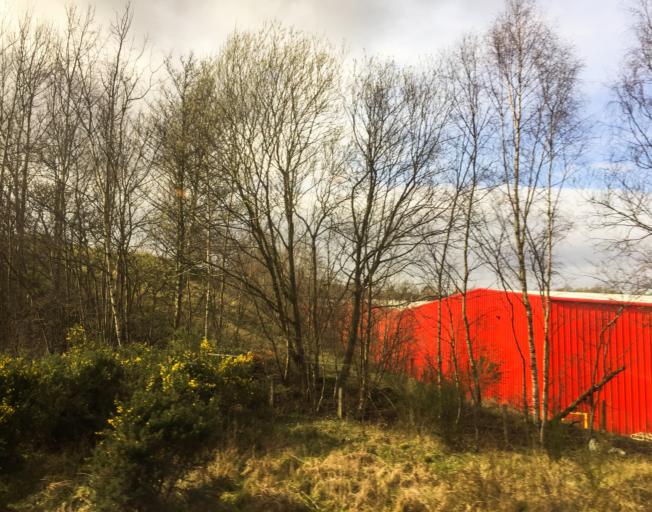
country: GB
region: Scotland
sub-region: East Dunbartonshire
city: Bearsden
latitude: 55.8956
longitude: -4.3061
